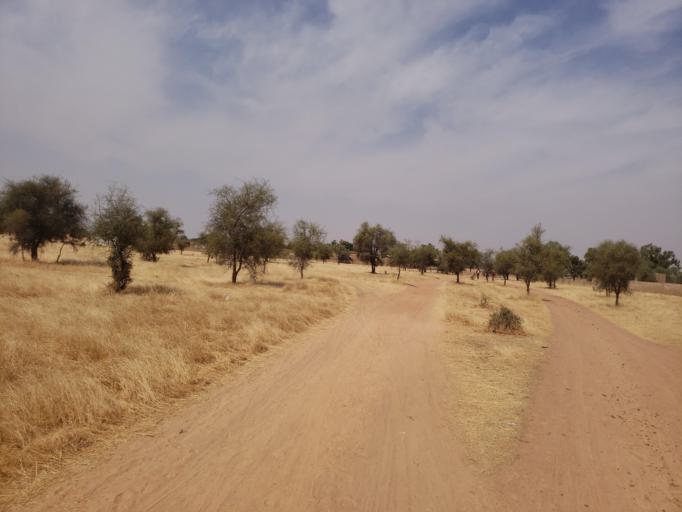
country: SN
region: Matam
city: Ranerou
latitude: 15.2924
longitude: -13.9630
